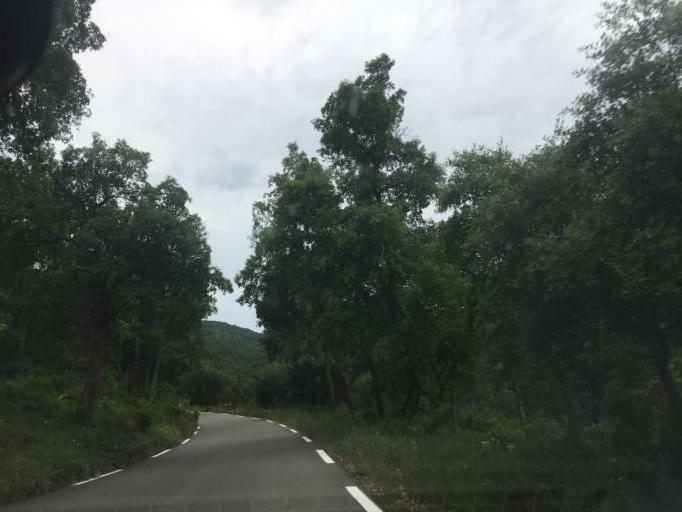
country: FR
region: Provence-Alpes-Cote d'Azur
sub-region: Departement du Var
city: Pierrefeu-du-Var
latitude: 43.2093
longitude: 6.2130
